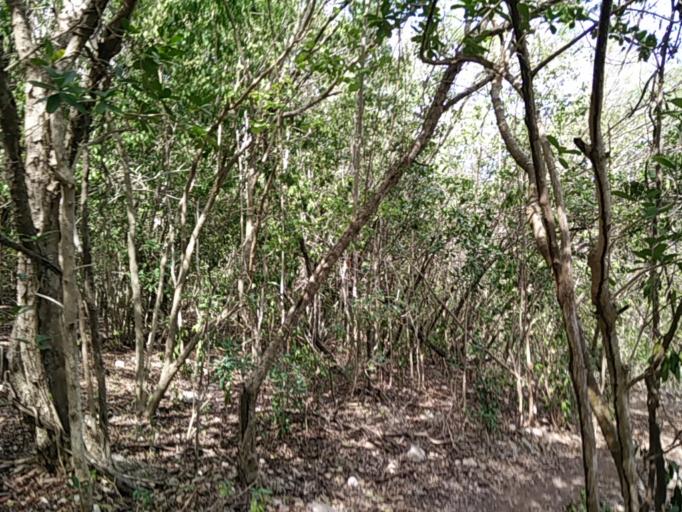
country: GP
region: Guadeloupe
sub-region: Guadeloupe
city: Sainte-Anne
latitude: 16.2108
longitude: -61.4273
